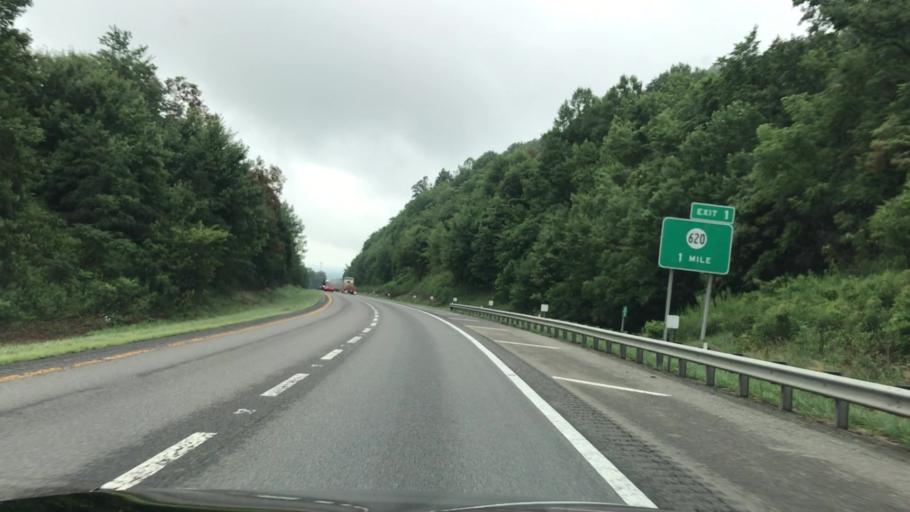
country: US
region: Virginia
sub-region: Carroll County
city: Cana
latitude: 36.5949
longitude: -80.7431
